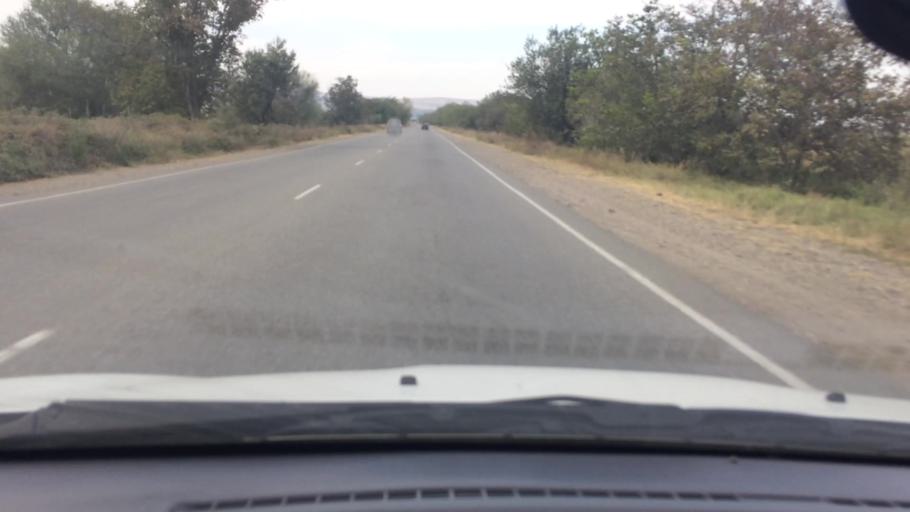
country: GE
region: Kvemo Kartli
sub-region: Marneuli
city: Marneuli
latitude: 41.5621
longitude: 44.7758
